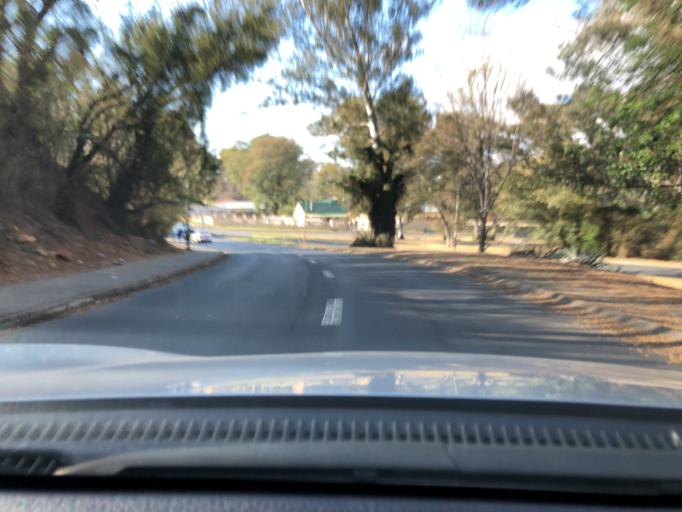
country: ZA
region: KwaZulu-Natal
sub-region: uThukela District Municipality
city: Ladysmith
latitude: -28.5585
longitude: 29.7743
